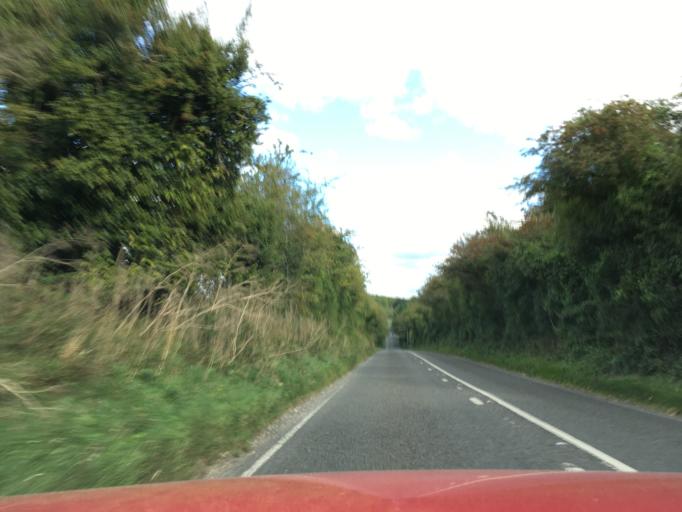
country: GB
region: England
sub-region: Hampshire
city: Abbotts Ann
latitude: 51.1164
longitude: -1.5230
